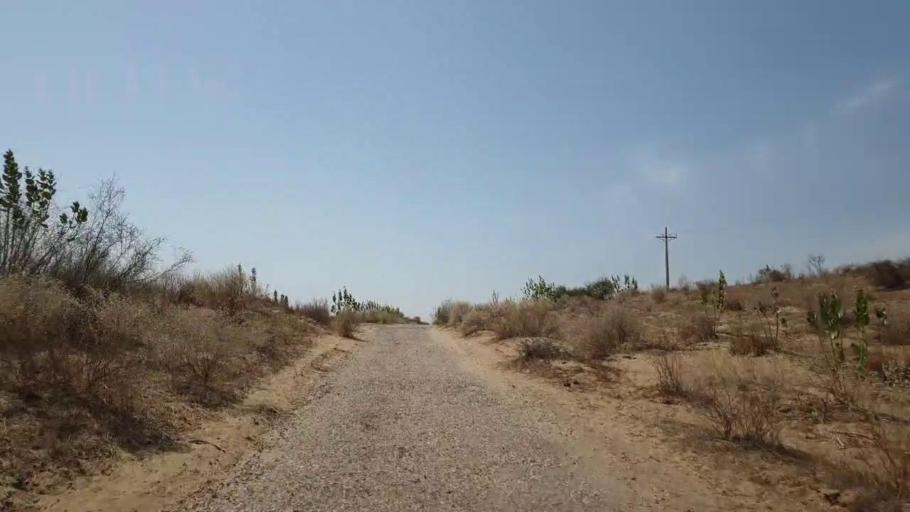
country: PK
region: Sindh
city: Umarkot
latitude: 25.2042
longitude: 69.9179
